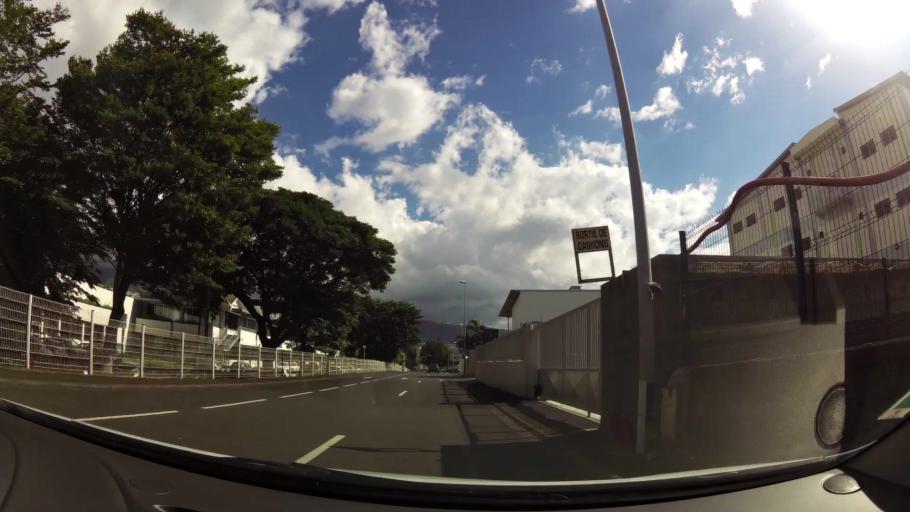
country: RE
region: Reunion
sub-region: Reunion
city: Saint-Denis
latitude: -20.8922
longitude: 55.4938
